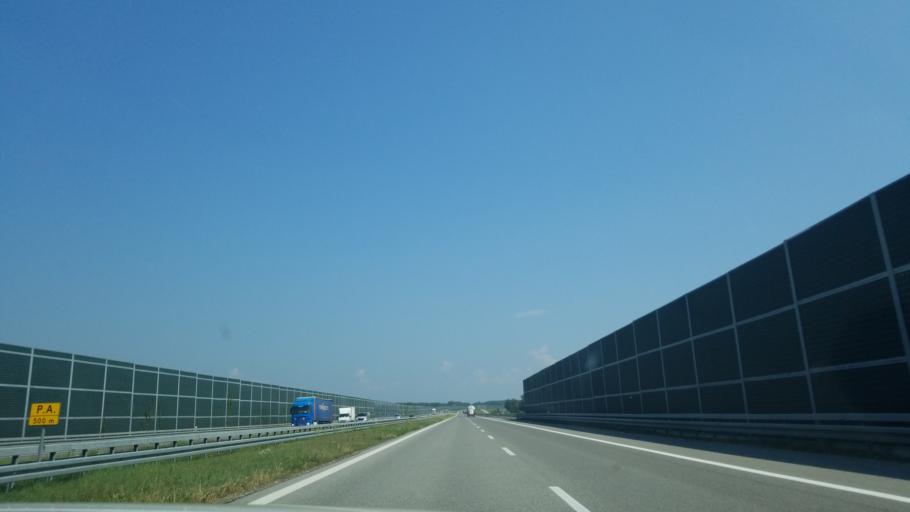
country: PL
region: Subcarpathian Voivodeship
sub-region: Powiat ropczycko-sedziszowski
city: Sedziszow Malopolski
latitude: 50.1108
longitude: 21.6923
